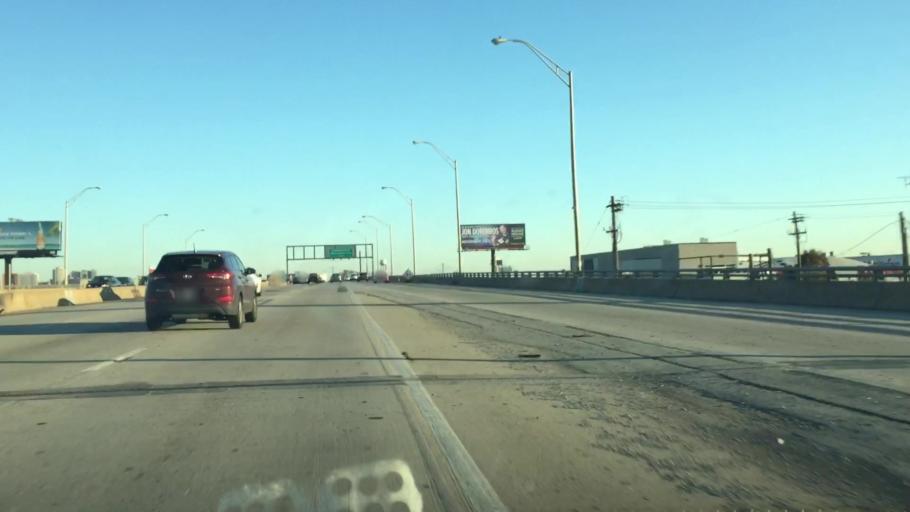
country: US
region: New Jersey
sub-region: Camden County
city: Camden
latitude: 39.9132
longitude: -75.1482
